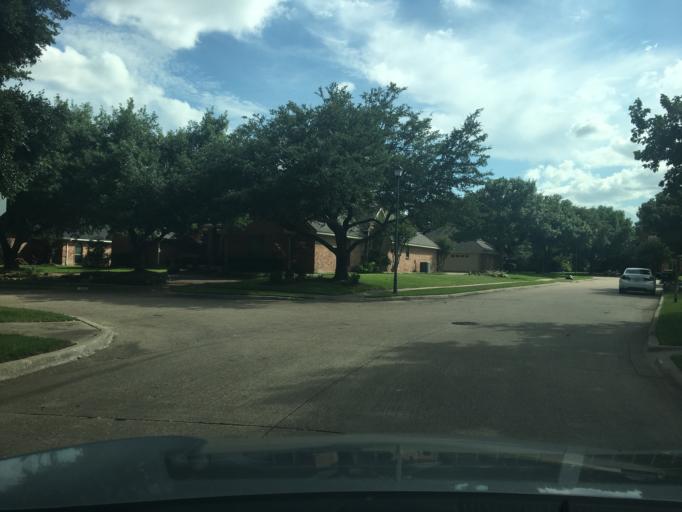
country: US
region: Texas
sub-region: Dallas County
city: Garland
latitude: 32.9368
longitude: -96.6767
